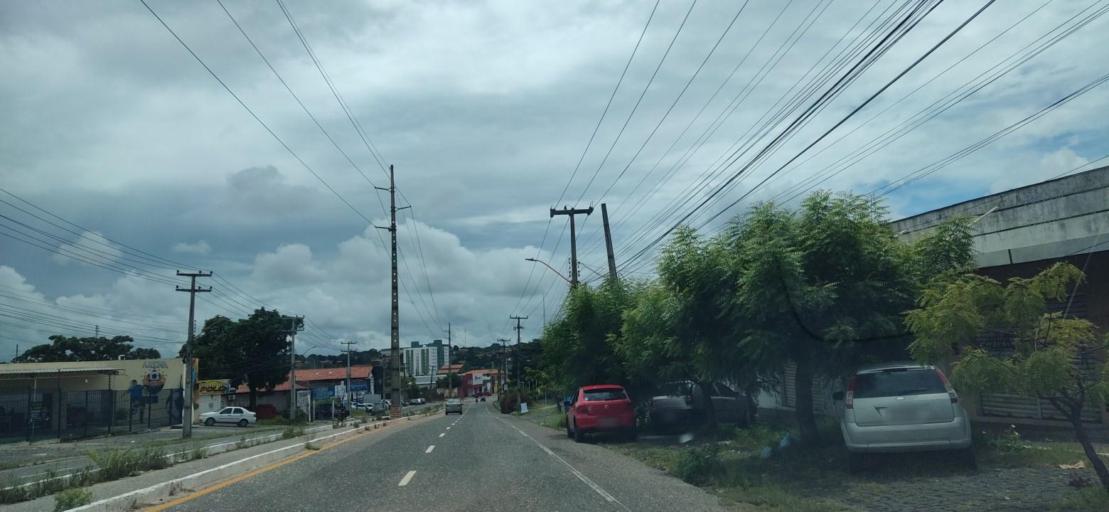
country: BR
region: Piaui
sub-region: Teresina
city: Teresina
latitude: -5.0617
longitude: -42.7563
